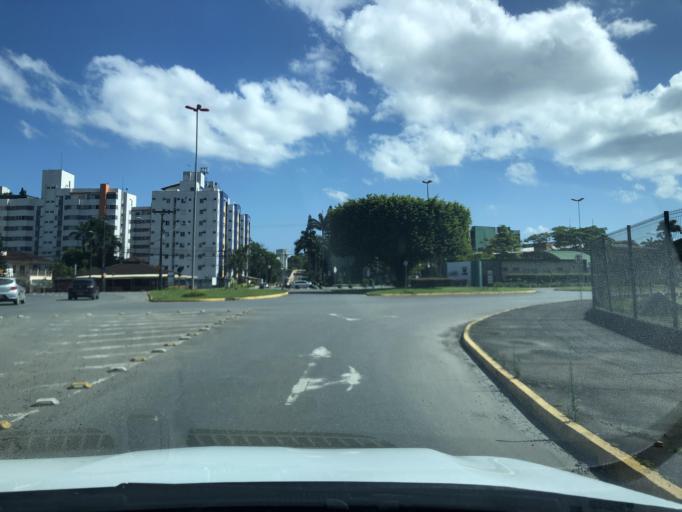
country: BR
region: Santa Catarina
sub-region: Joinville
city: Joinville
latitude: -26.2501
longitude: -48.8543
